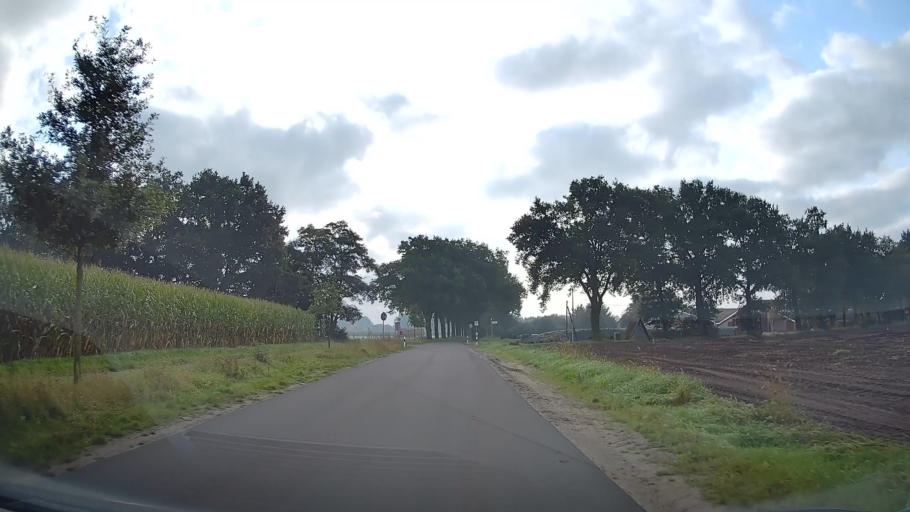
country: DE
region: Lower Saxony
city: Wardenburg
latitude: 53.0073
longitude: 8.1418
